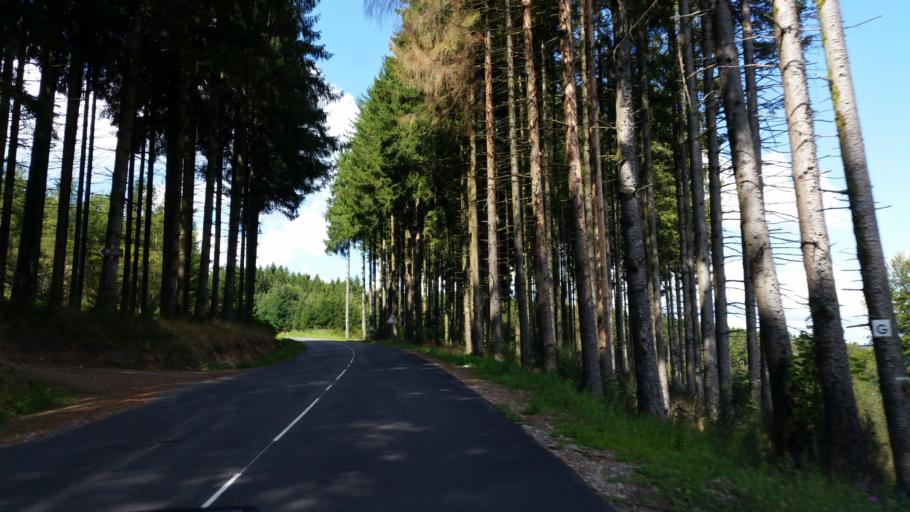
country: FR
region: Lorraine
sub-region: Departement des Vosges
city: Granges-sur-Vologne
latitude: 48.1190
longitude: 6.7802
